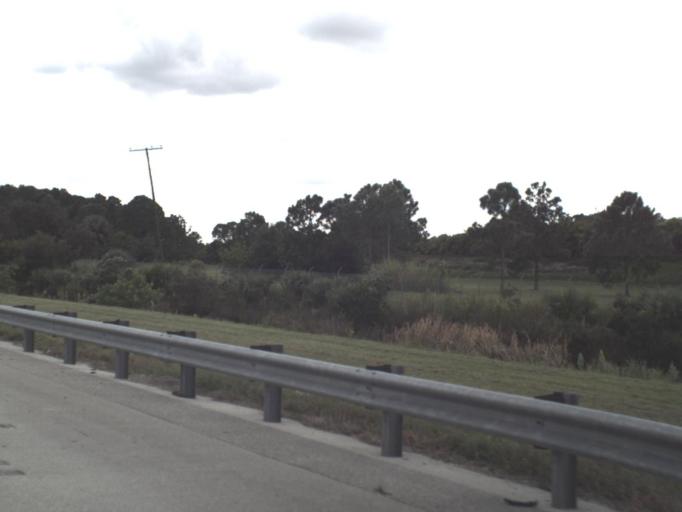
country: US
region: Florida
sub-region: Saint Lucie County
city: Port Saint Lucie
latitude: 27.3039
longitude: -80.3742
